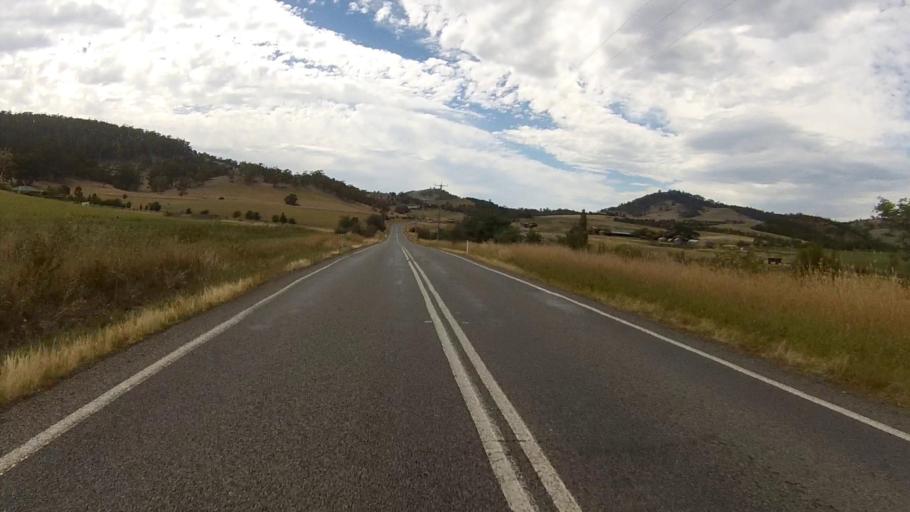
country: AU
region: Tasmania
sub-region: Sorell
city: Sorell
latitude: -42.6916
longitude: 147.4713
